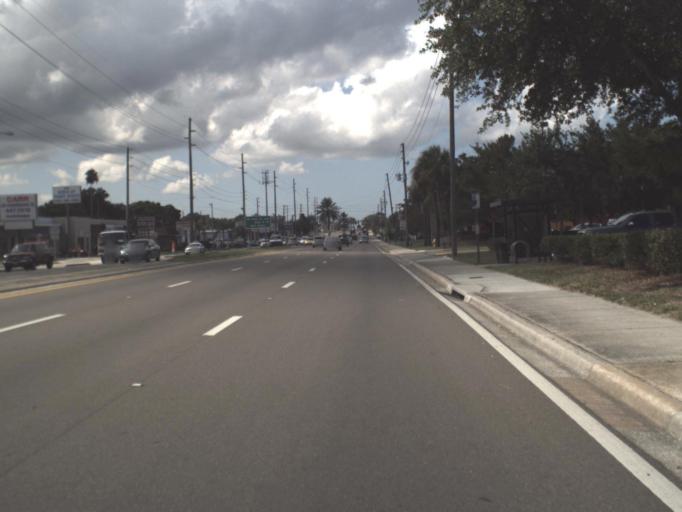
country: US
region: Florida
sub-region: Pinellas County
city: Belleair
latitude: 27.9386
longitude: -82.7875
